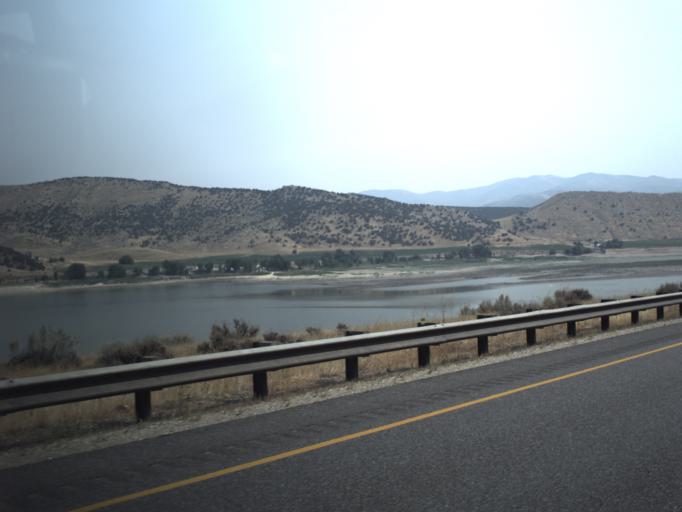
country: US
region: Utah
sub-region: Summit County
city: Coalville
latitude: 40.9419
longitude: -111.4130
